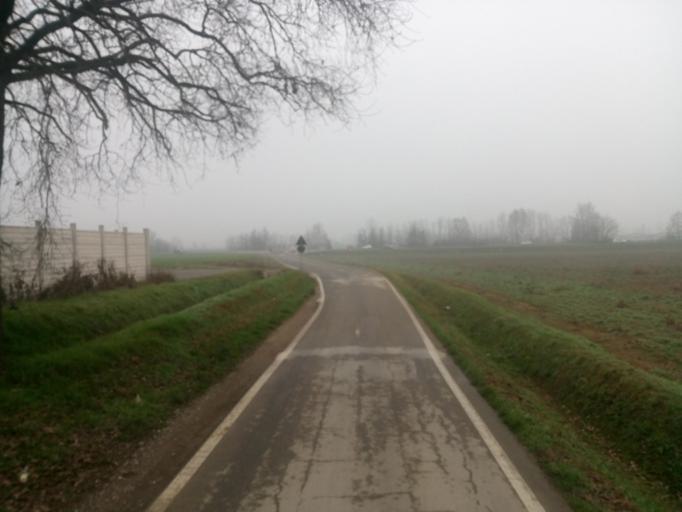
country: IT
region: Lombardy
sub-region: Provincia di Cremona
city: Spinadesco
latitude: 45.1606
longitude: 9.9217
